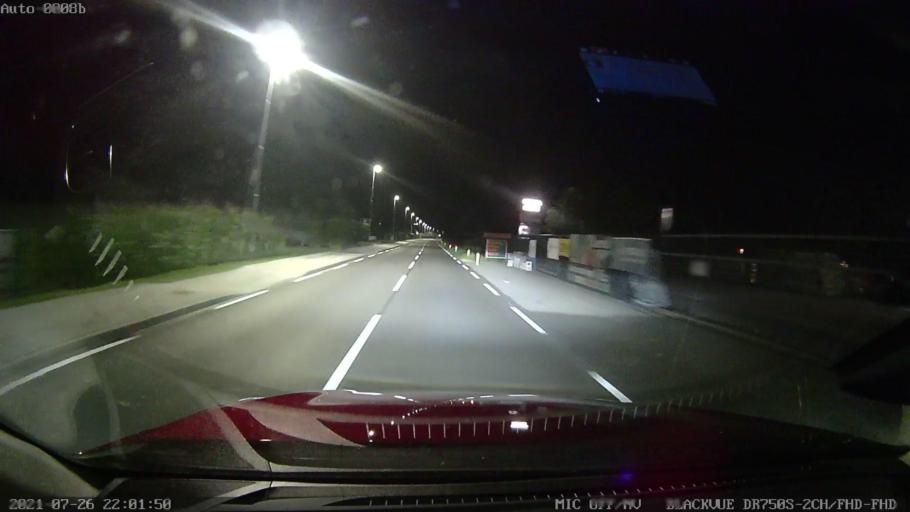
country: SI
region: Markovci
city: Markovci
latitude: 46.3858
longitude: 15.9629
